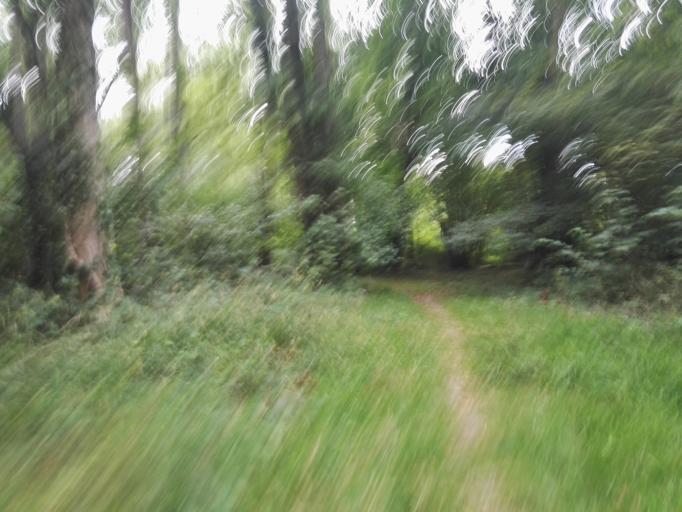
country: FR
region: Haute-Normandie
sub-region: Departement de l'Eure
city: Houlbec-Cocherel
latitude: 49.0670
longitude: 1.2993
